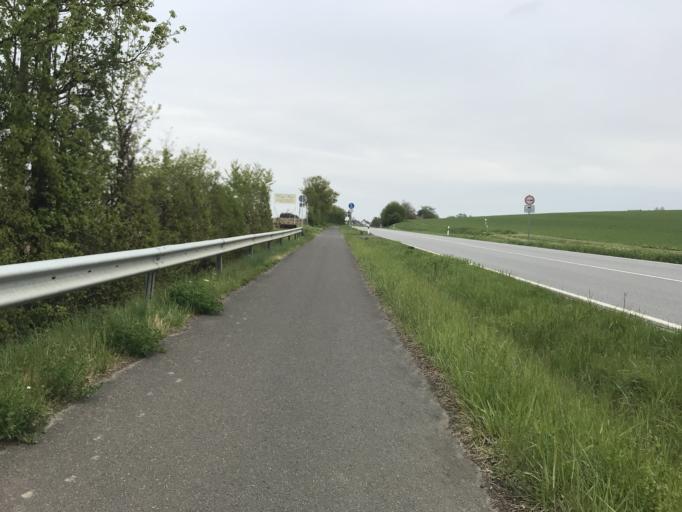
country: DE
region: Rheinland-Pfalz
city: Appenheim
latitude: 49.9372
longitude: 8.0266
